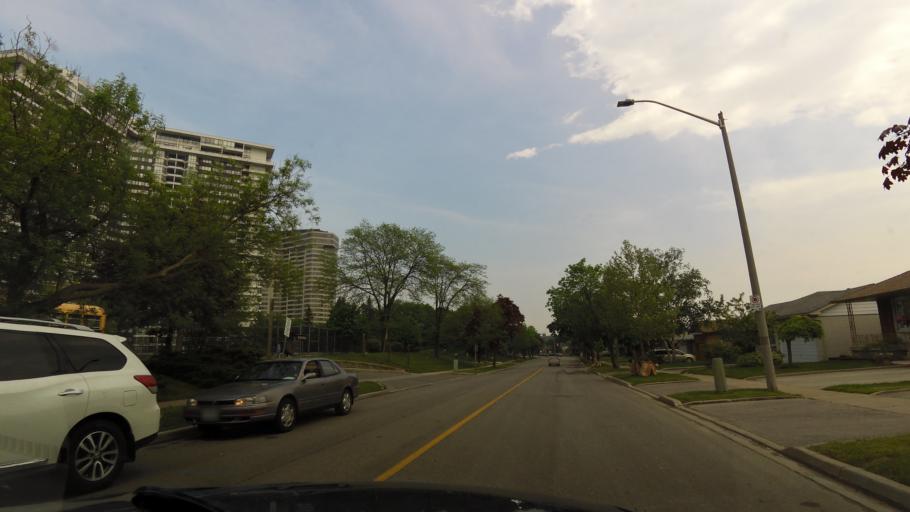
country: CA
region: Ontario
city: Etobicoke
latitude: 43.6162
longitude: -79.5986
